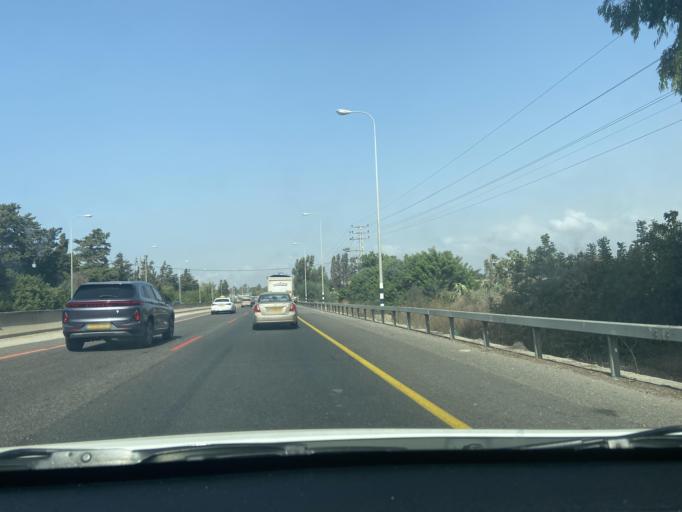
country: IL
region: Northern District
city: El Mazra`a
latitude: 32.9554
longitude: 35.0915
